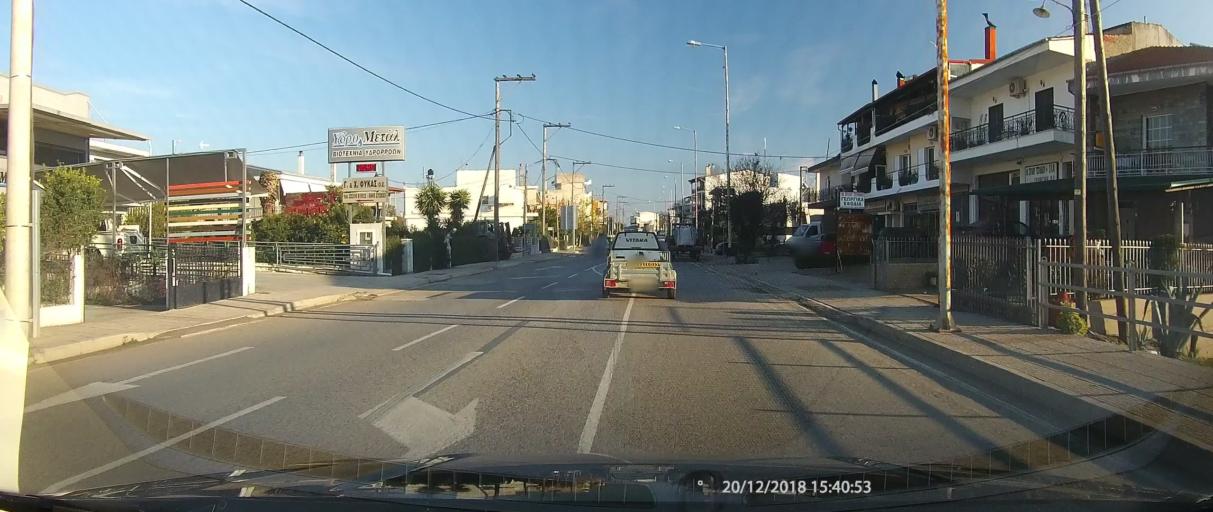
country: GR
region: Central Greece
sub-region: Nomos Fthiotidos
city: Stavros
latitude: 38.8919
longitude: 22.3786
